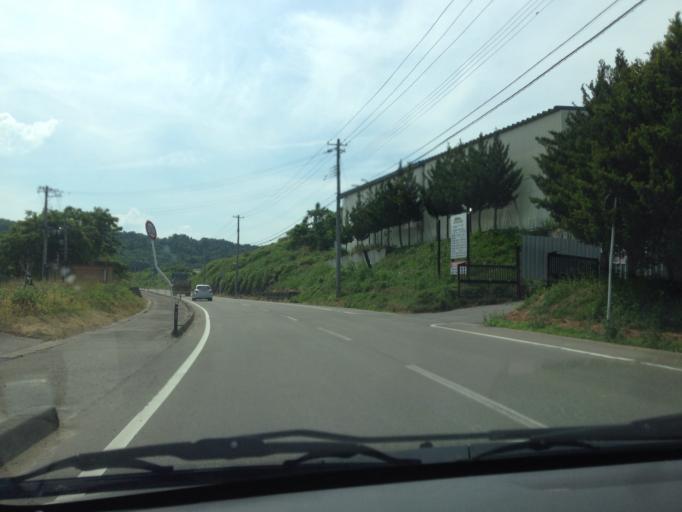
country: JP
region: Fukushima
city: Kitakata
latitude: 37.6137
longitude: 139.8064
